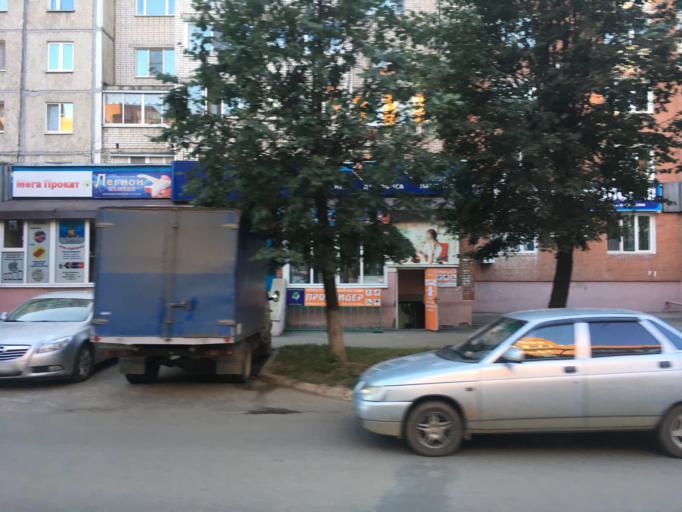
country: RU
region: Mariy-El
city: Yoshkar-Ola
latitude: 56.6426
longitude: 47.8900
